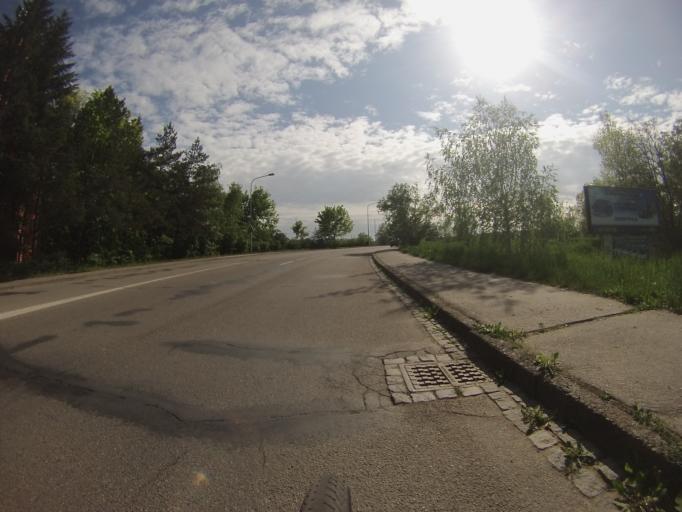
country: CZ
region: South Moravian
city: Troubsko
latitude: 49.2274
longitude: 16.5214
